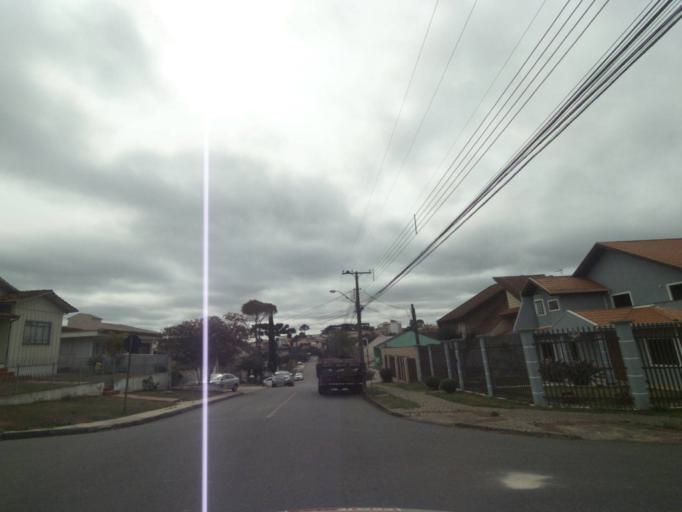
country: BR
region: Parana
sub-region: Pinhais
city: Pinhais
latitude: -25.4759
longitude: -49.2345
